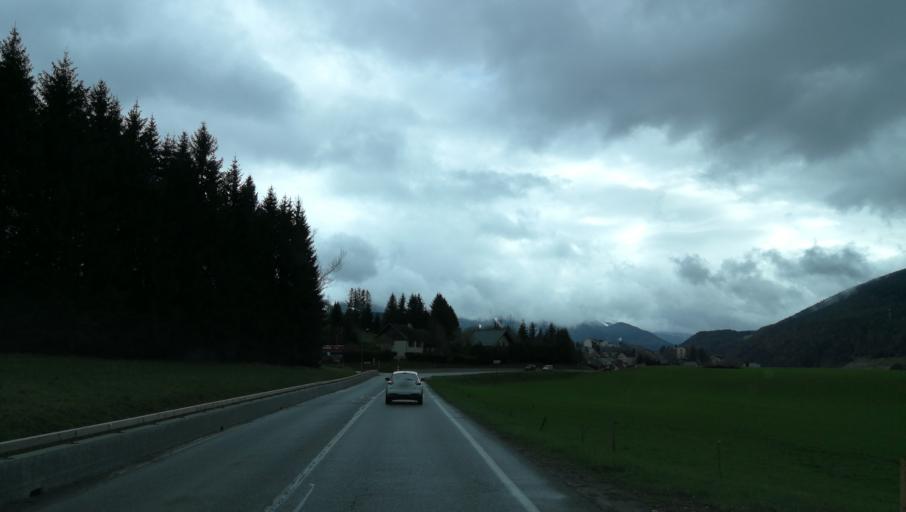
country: FR
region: Rhone-Alpes
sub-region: Departement de l'Isere
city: Villard-de-Lans
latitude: 45.0829
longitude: 5.5538
